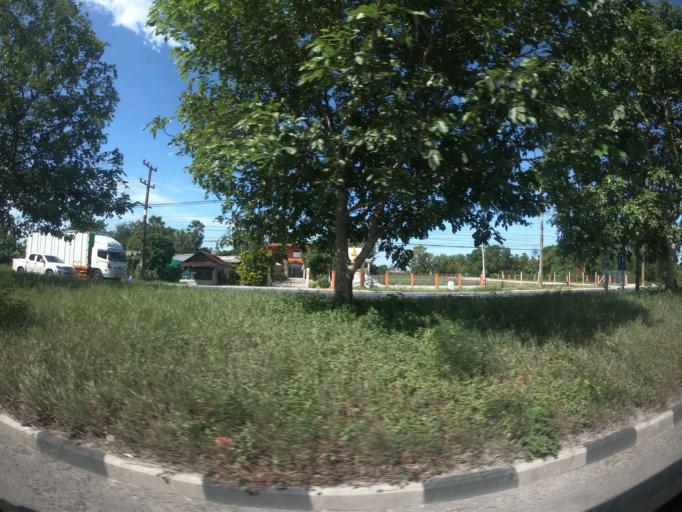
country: TH
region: Nakhon Nayok
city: Ban Na
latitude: 14.2505
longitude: 101.0996
